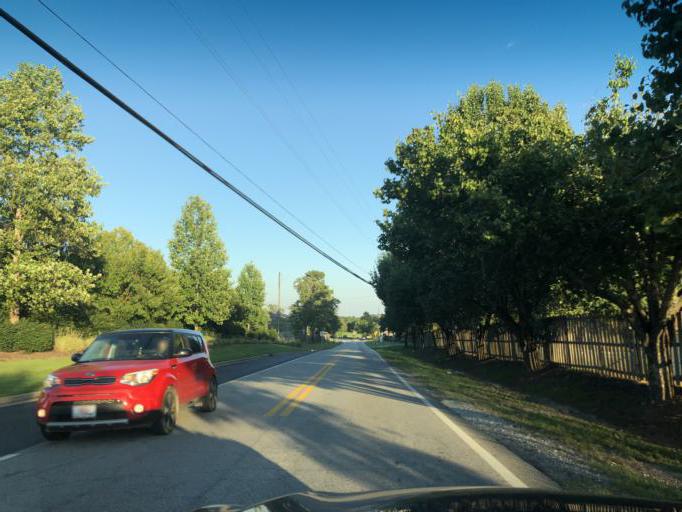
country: US
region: Georgia
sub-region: Muscogee County
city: Columbus
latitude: 32.5481
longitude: -84.8926
